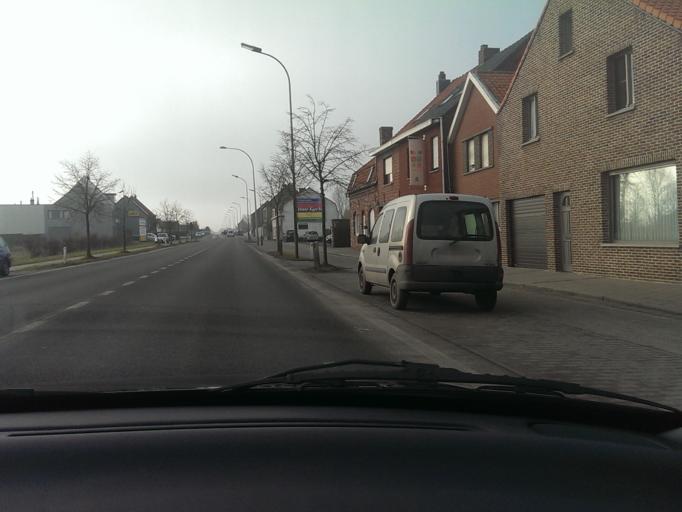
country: BE
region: Flanders
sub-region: Provincie West-Vlaanderen
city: Ledegem
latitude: 50.8488
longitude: 3.1105
